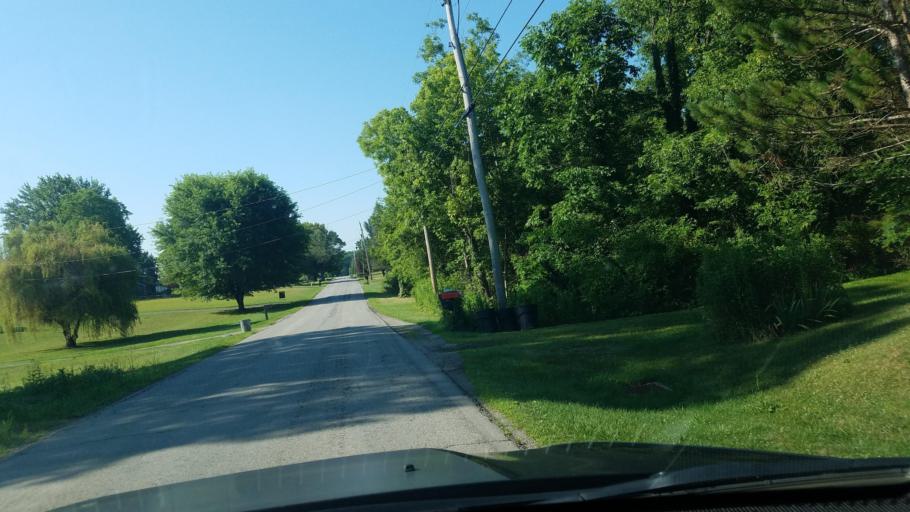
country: US
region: Ohio
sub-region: Trumbull County
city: Champion Heights
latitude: 41.2977
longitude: -80.8206
